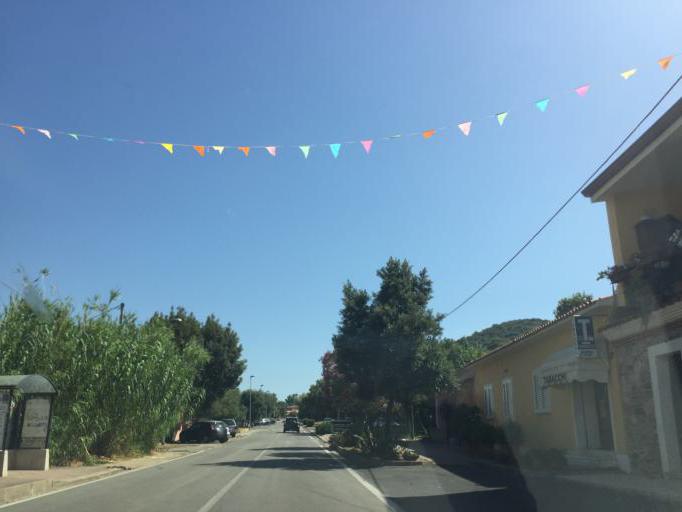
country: IT
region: Sardinia
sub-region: Provincia di Olbia-Tempio
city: San Teodoro
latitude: 40.7443
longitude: 9.6466
